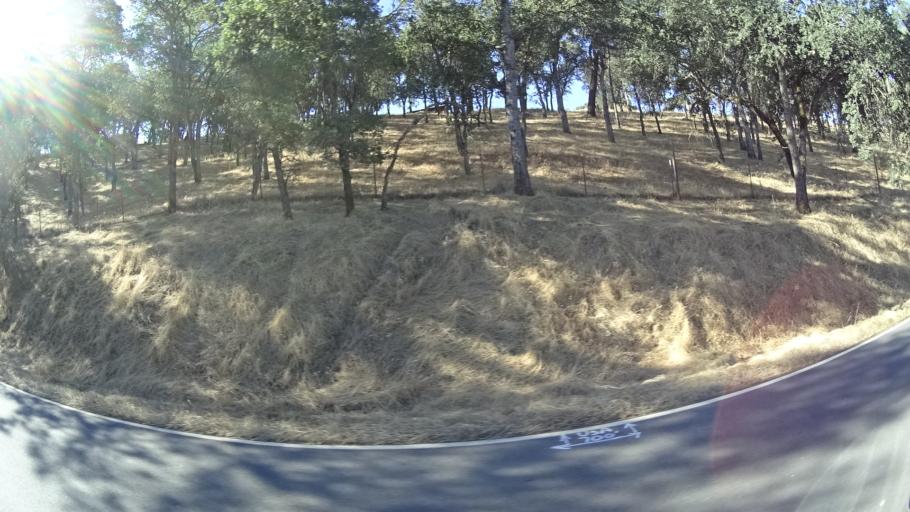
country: US
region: California
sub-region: Calaveras County
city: Rancho Calaveras
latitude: 38.1212
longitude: -120.8706
